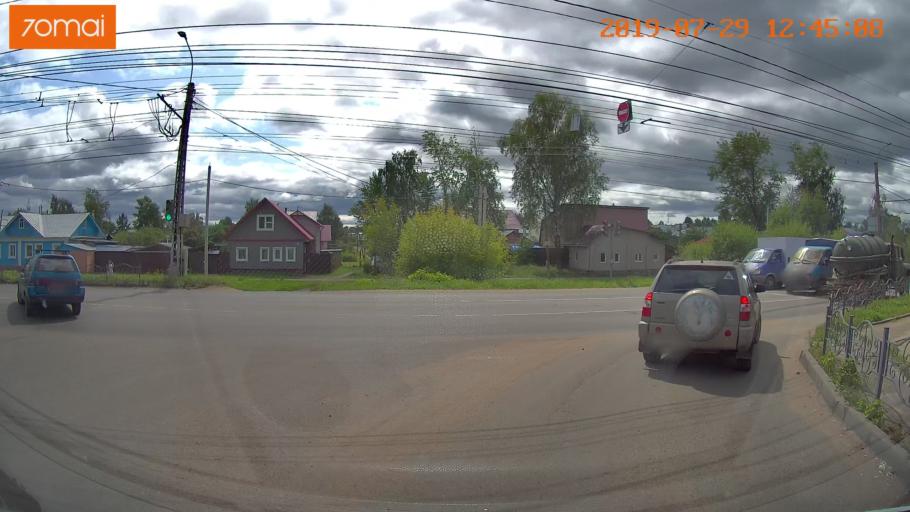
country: RU
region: Ivanovo
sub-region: Gorod Ivanovo
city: Ivanovo
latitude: 56.9998
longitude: 40.9304
